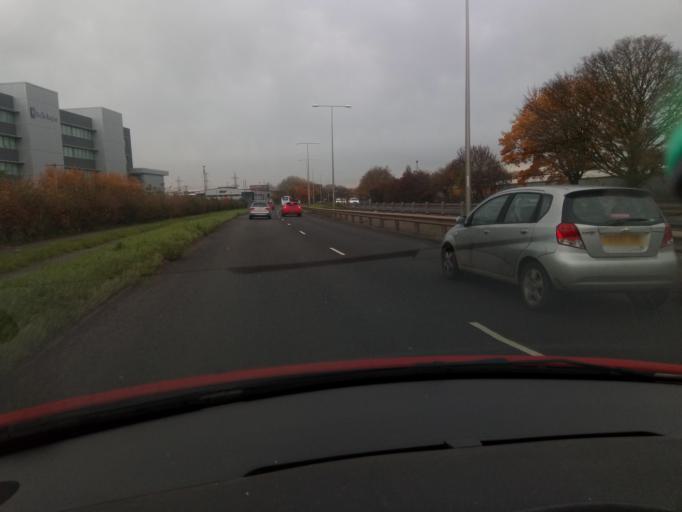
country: GB
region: England
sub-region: Derbyshire
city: Borrowash
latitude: 52.9073
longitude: -1.4310
